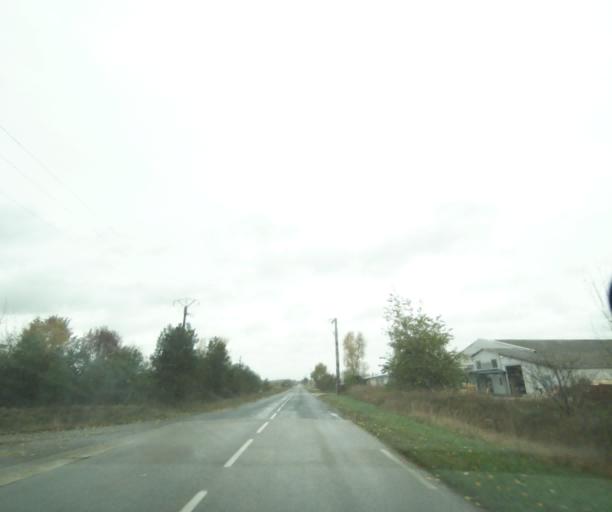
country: FR
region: Rhone-Alpes
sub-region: Departement de l'Ain
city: Loyettes
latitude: 45.7920
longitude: 5.2101
